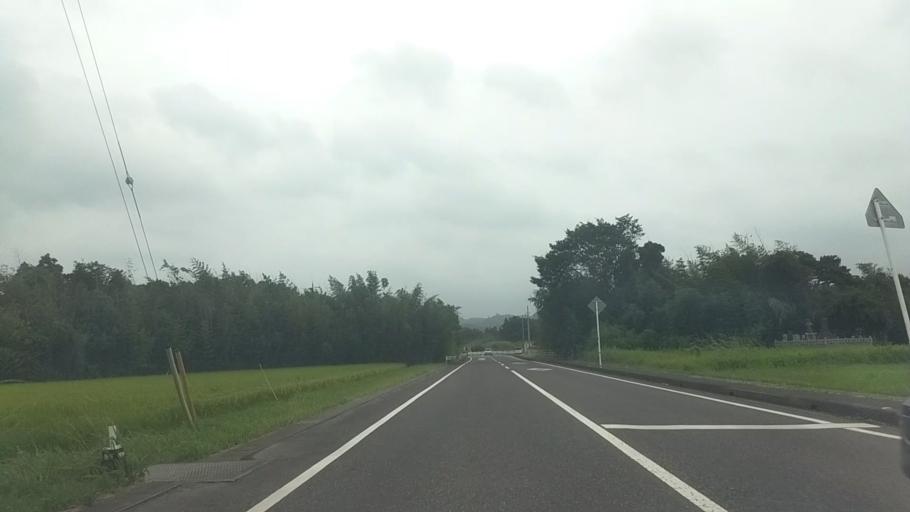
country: JP
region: Chiba
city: Kimitsu
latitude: 35.2190
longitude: 139.9166
